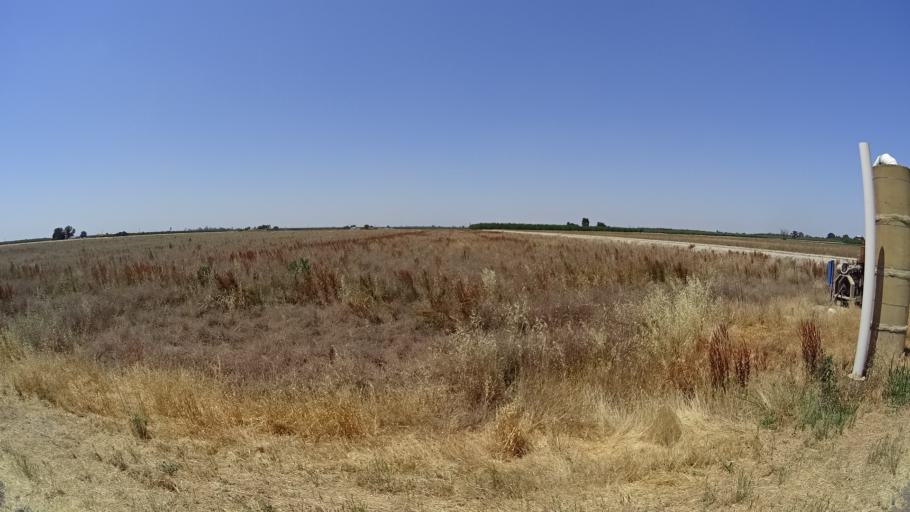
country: US
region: California
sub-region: Fresno County
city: Laton
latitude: 36.3902
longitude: -119.7270
